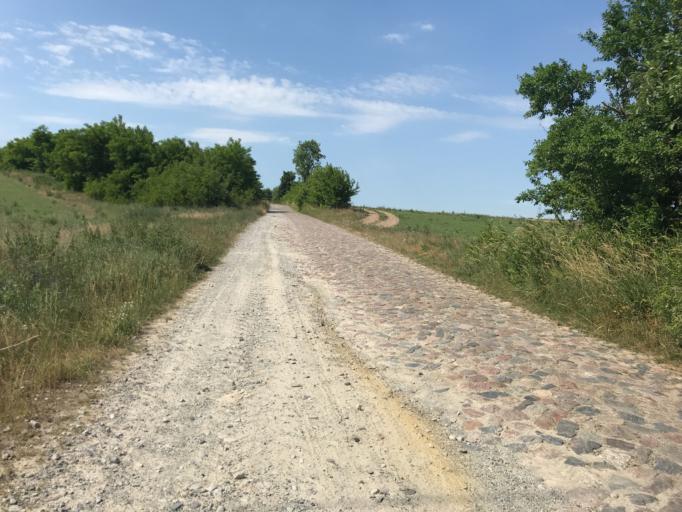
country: PL
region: West Pomeranian Voivodeship
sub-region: Powiat mysliborski
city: Debno
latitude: 52.7087
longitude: 14.6403
